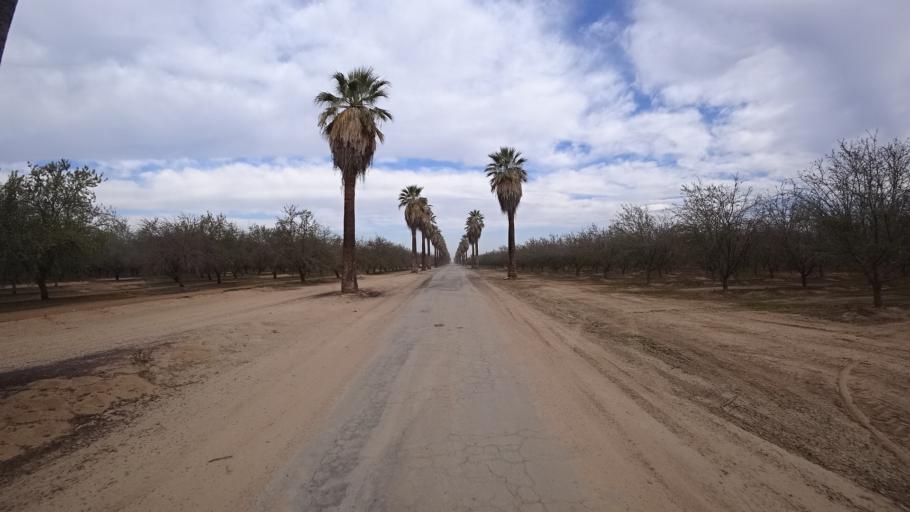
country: US
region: California
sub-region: Kern County
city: Rosedale
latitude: 35.4291
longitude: -119.1721
